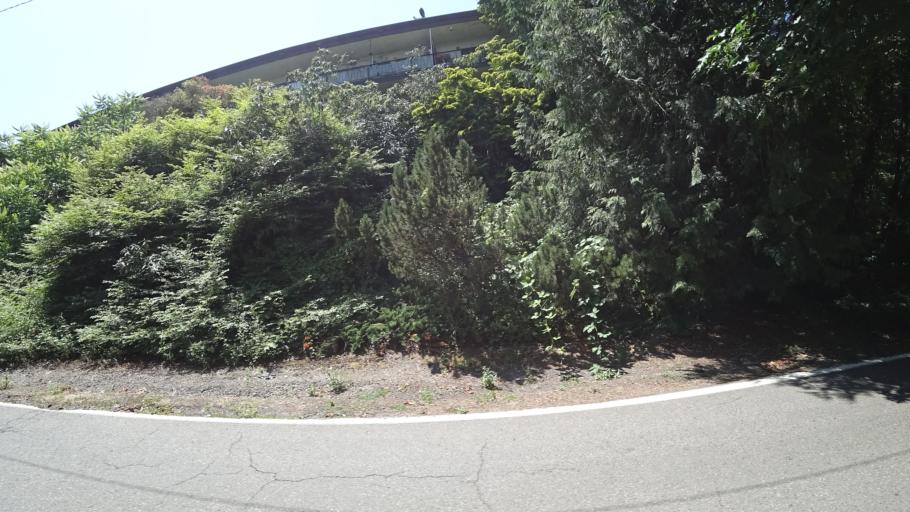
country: US
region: Oregon
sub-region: Multnomah County
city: Portland
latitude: 45.4888
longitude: -122.6808
